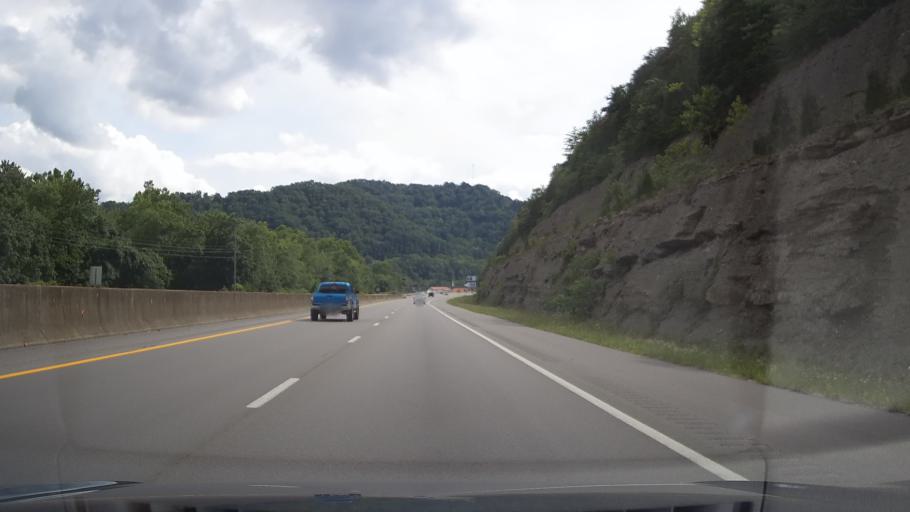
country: US
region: Kentucky
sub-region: Pike County
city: Coal Run Village
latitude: 37.5352
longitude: -82.6172
